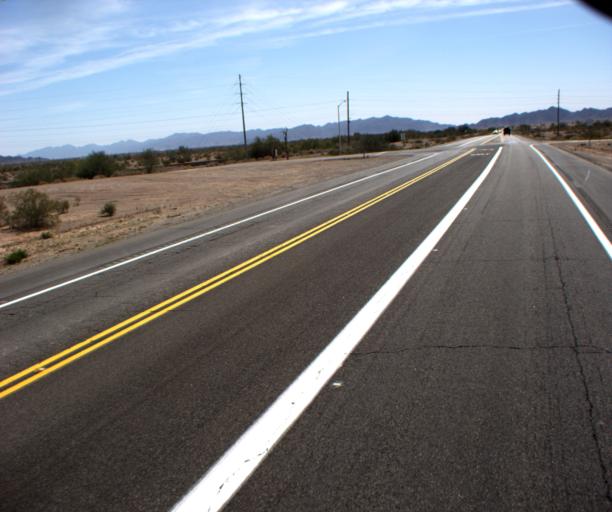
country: US
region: Arizona
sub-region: Yuma County
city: Fortuna Foothills
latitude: 32.8663
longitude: -114.3563
